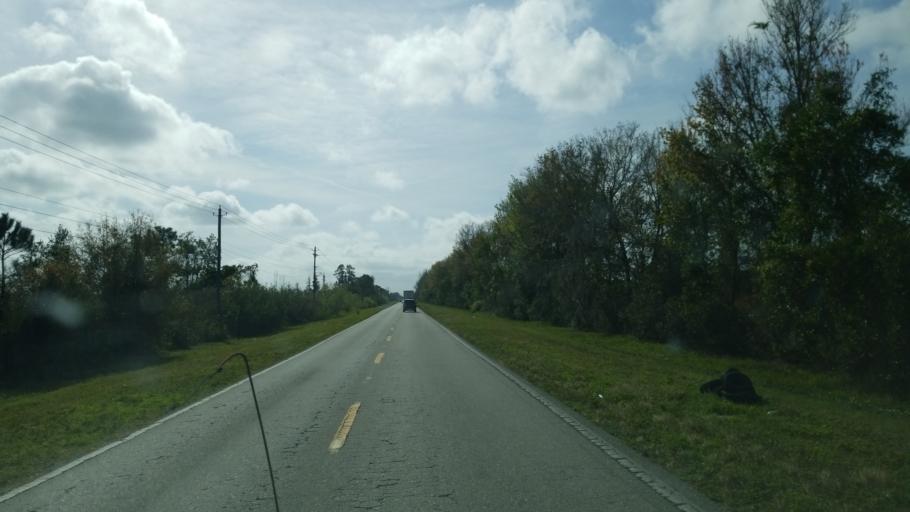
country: US
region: Florida
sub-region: Polk County
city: Polk City
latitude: 28.1986
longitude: -81.7523
